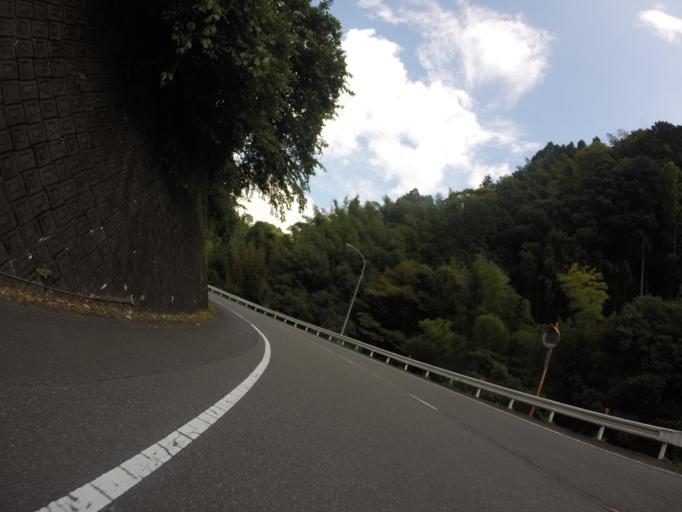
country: JP
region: Shizuoka
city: Shizuoka-shi
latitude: 35.1002
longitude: 138.4660
